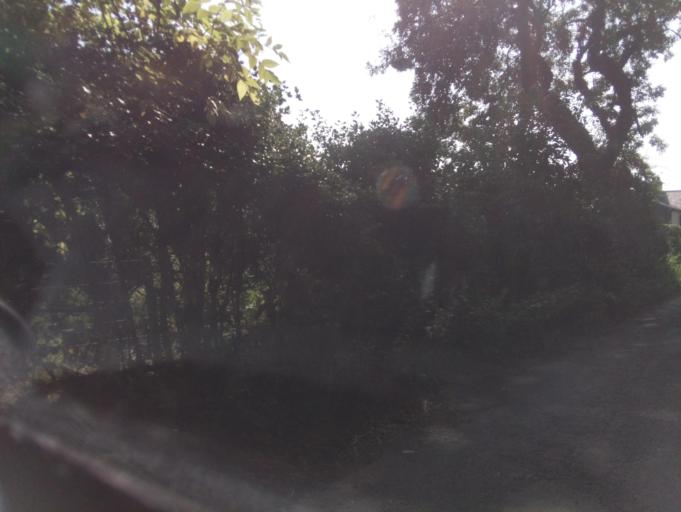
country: GB
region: England
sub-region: Derbyshire
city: Duffield
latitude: 52.9713
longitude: -1.5157
